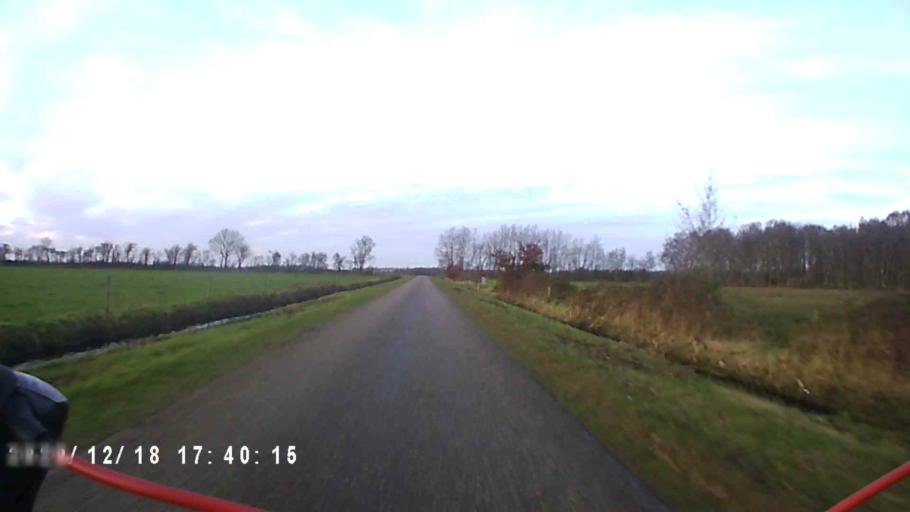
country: NL
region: Drenthe
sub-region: Gemeente Tynaarlo
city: Vries
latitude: 53.0922
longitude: 6.5807
